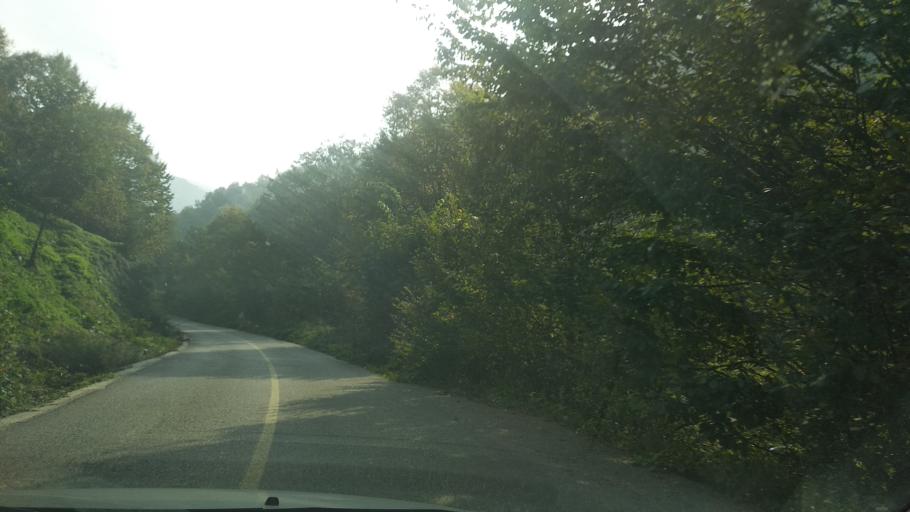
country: TR
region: Duzce
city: Kaynasli
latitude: 40.7070
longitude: 31.2647
